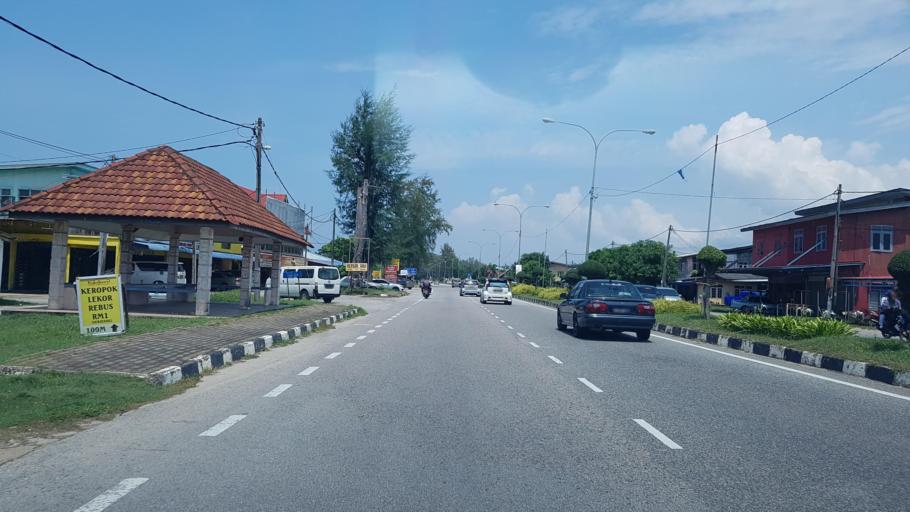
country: MY
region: Terengganu
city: Kuala Terengganu
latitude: 5.2972
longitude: 103.1658
